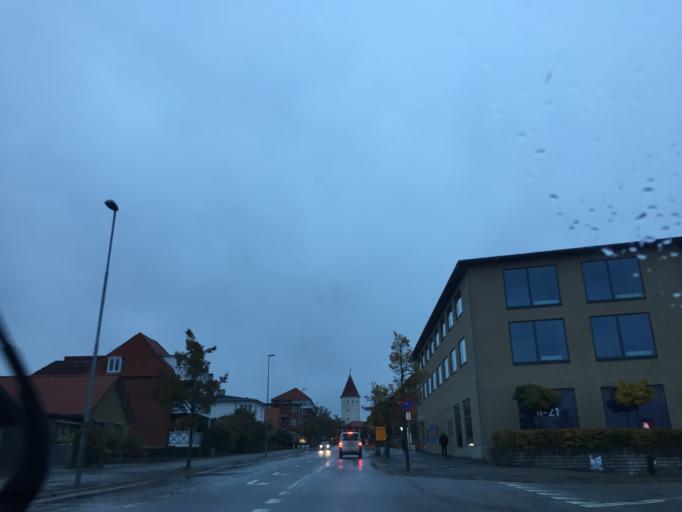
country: DK
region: Zealand
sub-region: Ringsted Kommune
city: Ringsted
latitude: 55.4420
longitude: 11.7861
